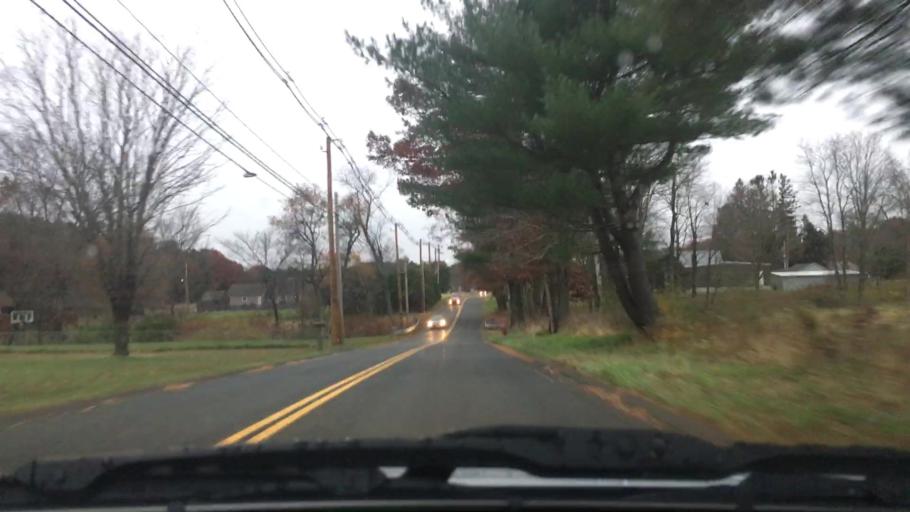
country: US
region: Massachusetts
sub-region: Hampden County
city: Westfield
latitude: 42.1110
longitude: -72.7843
